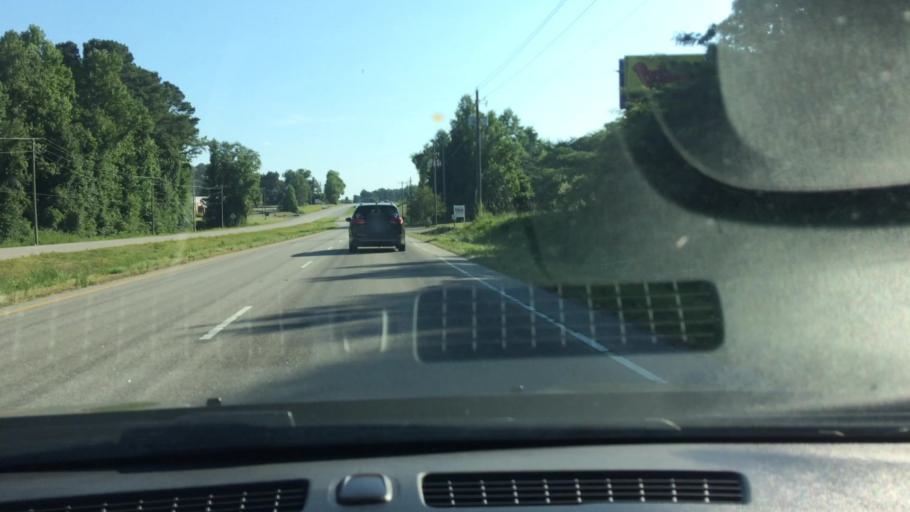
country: US
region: North Carolina
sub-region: Lenoir County
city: Kinston
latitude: 35.2933
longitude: -77.5439
